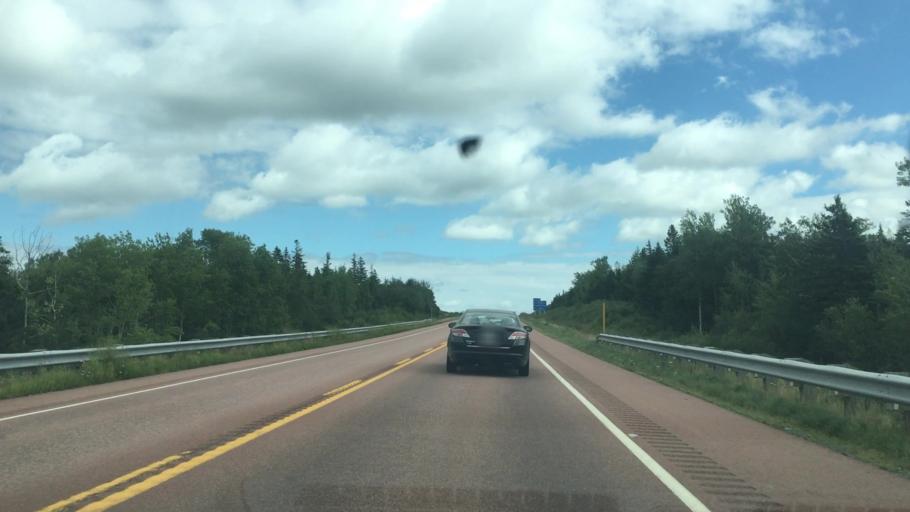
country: CA
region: Nova Scotia
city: Antigonish
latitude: 45.6057
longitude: -61.6771
